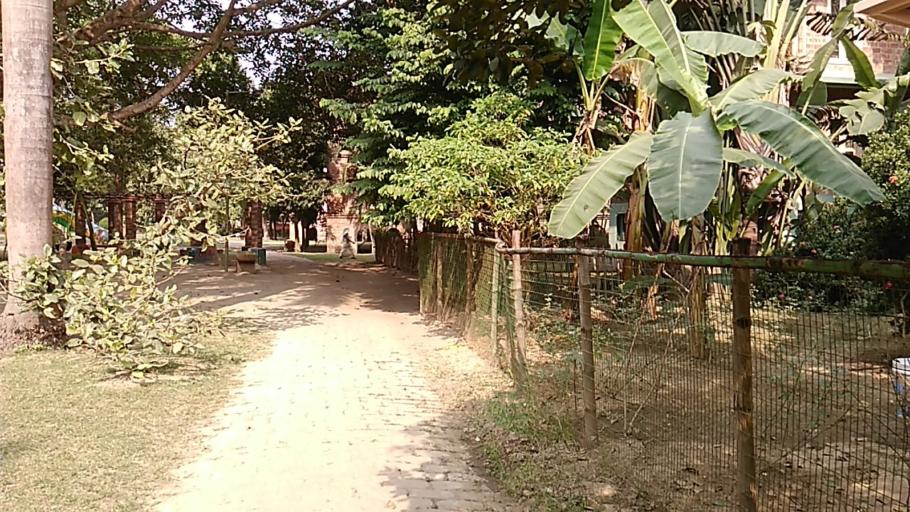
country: IN
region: West Bengal
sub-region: Nadia
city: Navadwip
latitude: 23.4213
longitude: 88.3882
